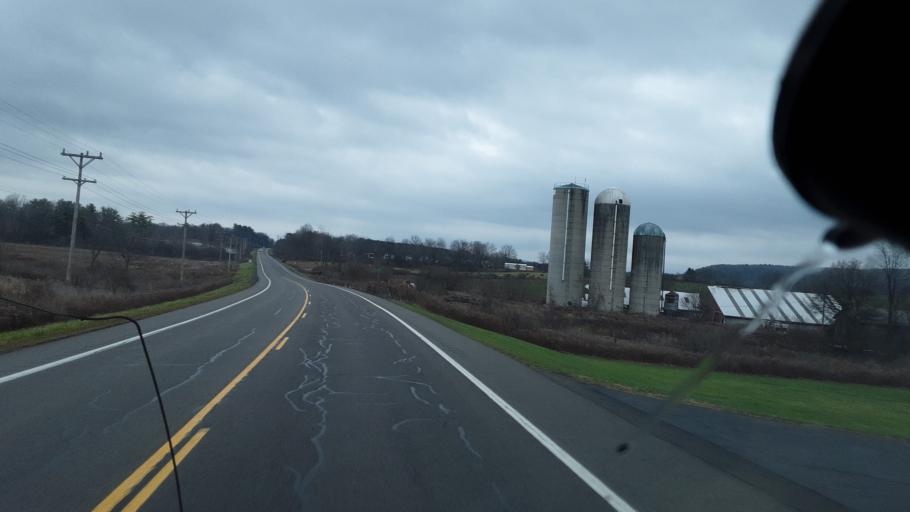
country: US
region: New York
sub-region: Allegany County
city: Houghton
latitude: 42.3890
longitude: -78.2072
